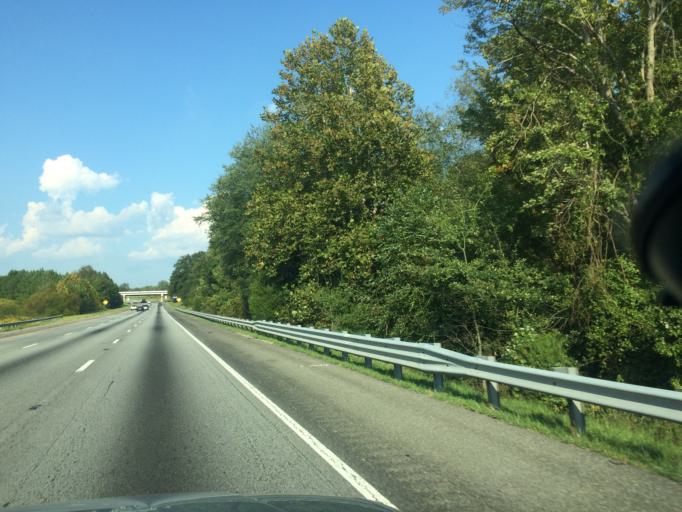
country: US
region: South Carolina
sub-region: Anderson County
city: Piedmont
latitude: 34.6887
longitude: -82.5102
